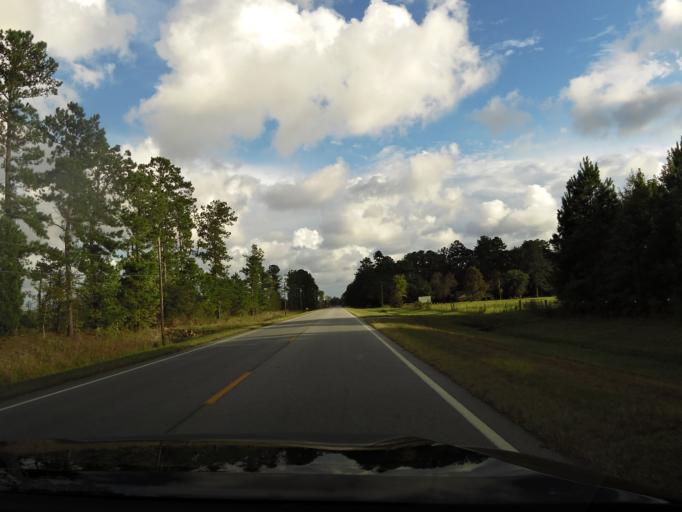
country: US
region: Georgia
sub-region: Liberty County
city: Midway
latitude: 31.7611
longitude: -81.4459
